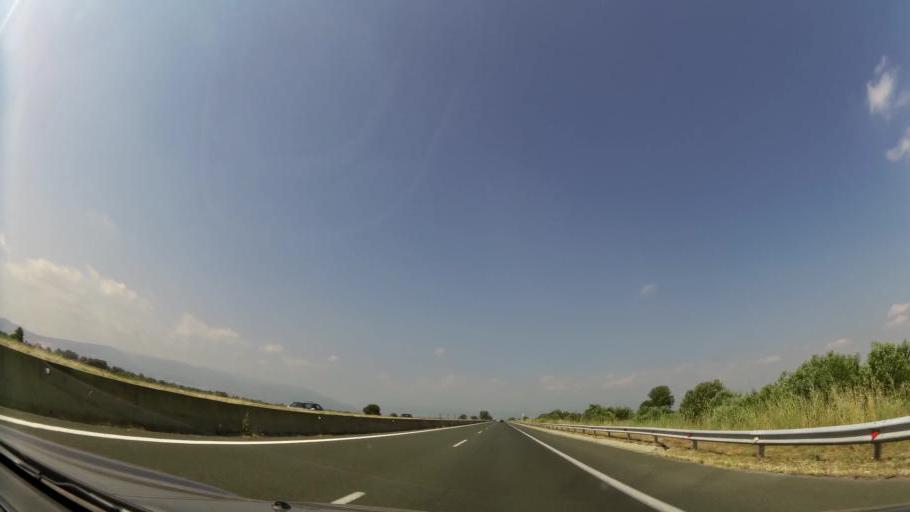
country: GR
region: Central Macedonia
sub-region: Nomos Imathias
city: Loutros
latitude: 40.5664
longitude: 22.3752
